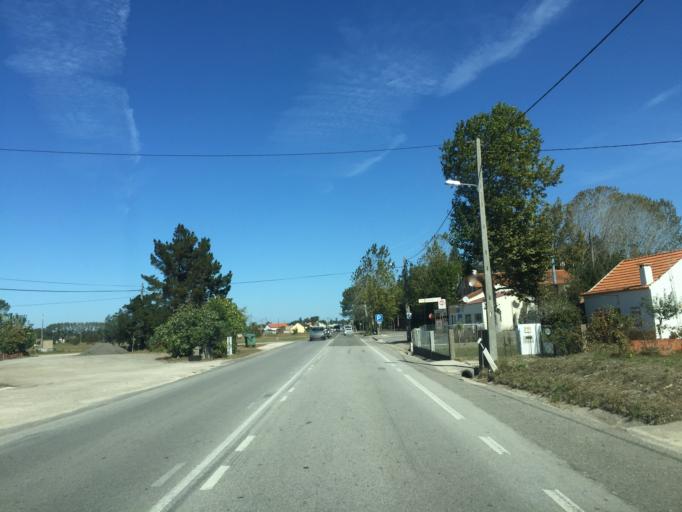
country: PT
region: Coimbra
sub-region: Figueira da Foz
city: Alhadas
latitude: 40.2370
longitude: -8.7951
